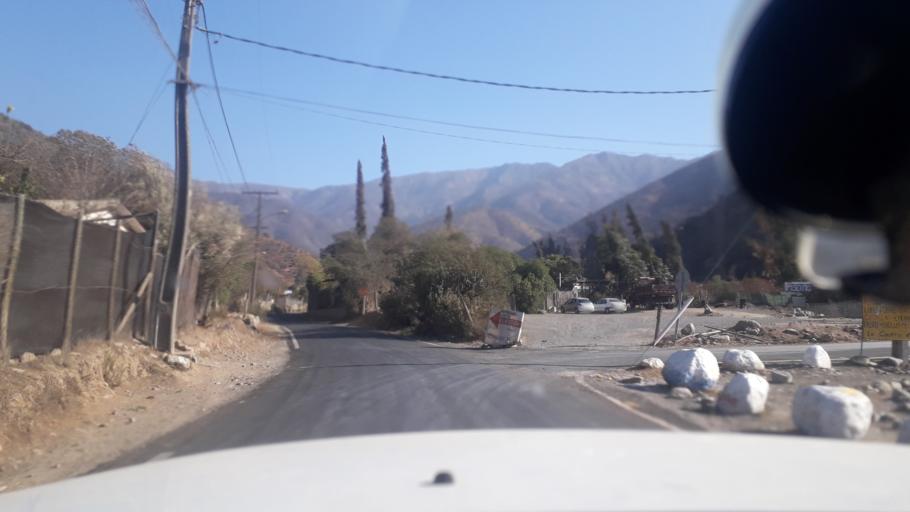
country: CL
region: Valparaiso
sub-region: Provincia de Marga Marga
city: Limache
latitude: -33.0538
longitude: -71.1116
